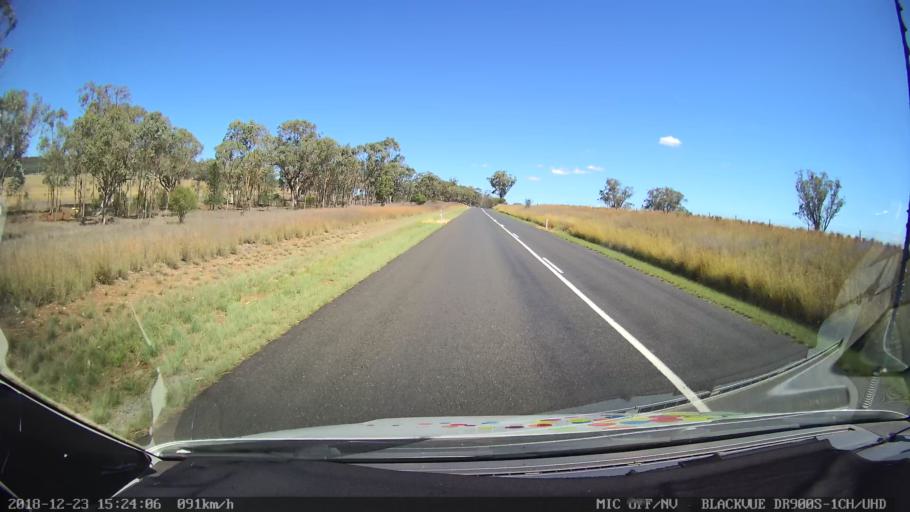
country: AU
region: New South Wales
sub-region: Tamworth Municipality
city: Manilla
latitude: -30.8879
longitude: 150.8206
